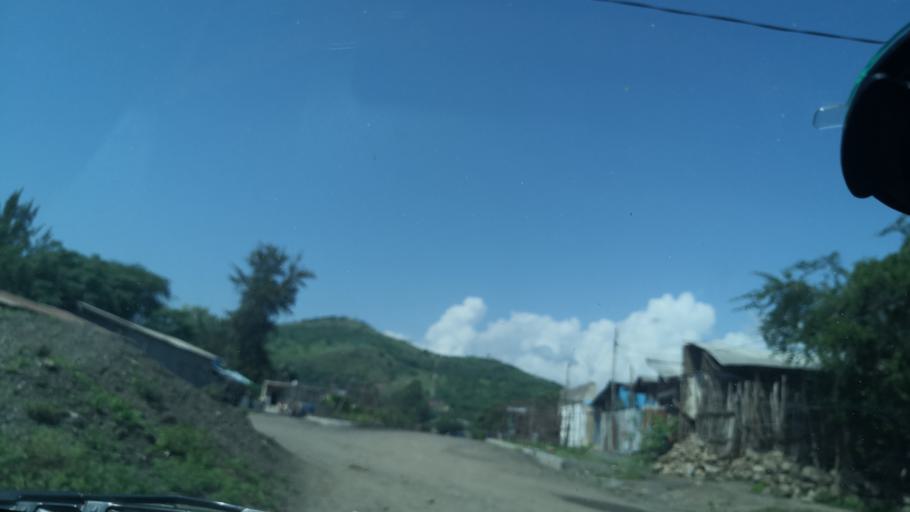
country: ET
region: Amhara
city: Abomsa
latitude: 10.3404
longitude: 39.9610
